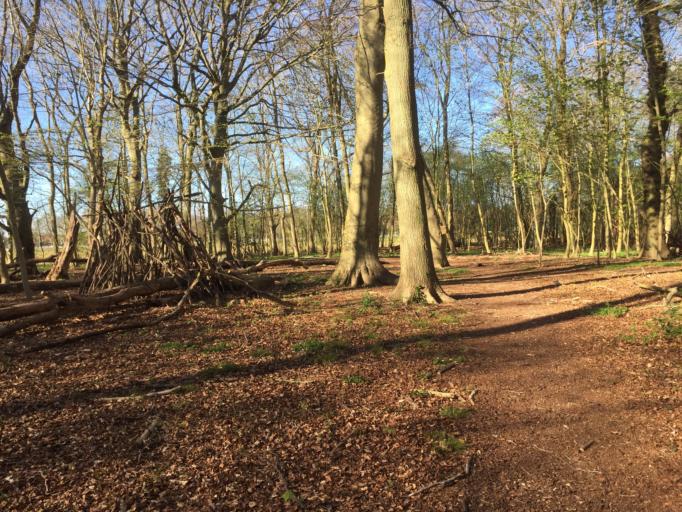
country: DK
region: South Denmark
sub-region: Odense Kommune
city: Neder Holluf
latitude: 55.3722
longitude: 10.4206
